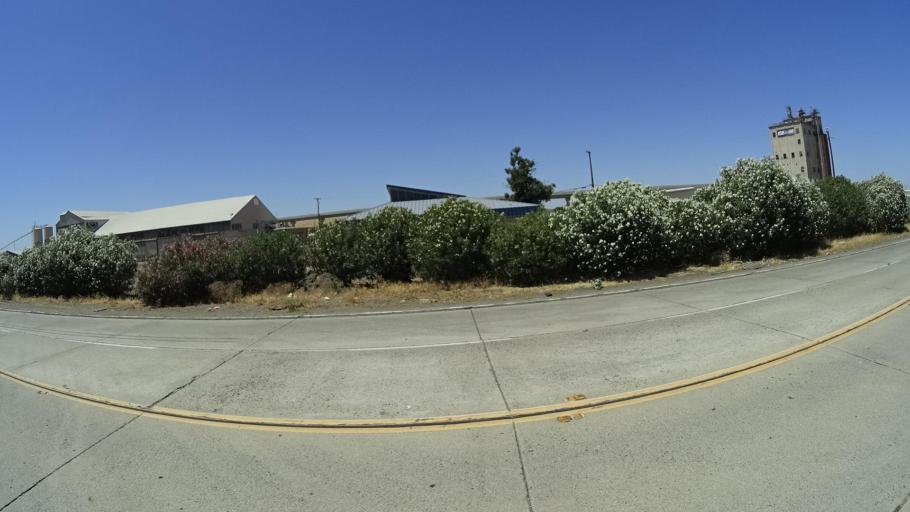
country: US
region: California
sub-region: Fresno County
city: Fresno
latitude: 36.6958
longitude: -119.7537
